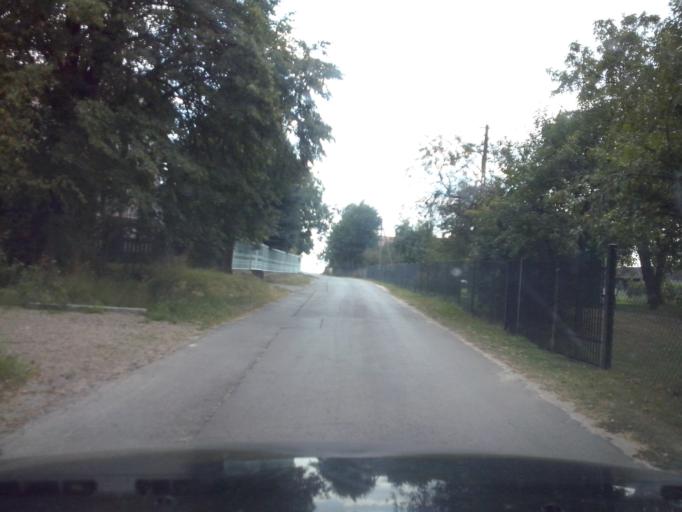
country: PL
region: Swietokrzyskie
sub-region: Powiat staszowski
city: Staszow
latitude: 50.5637
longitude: 21.1207
